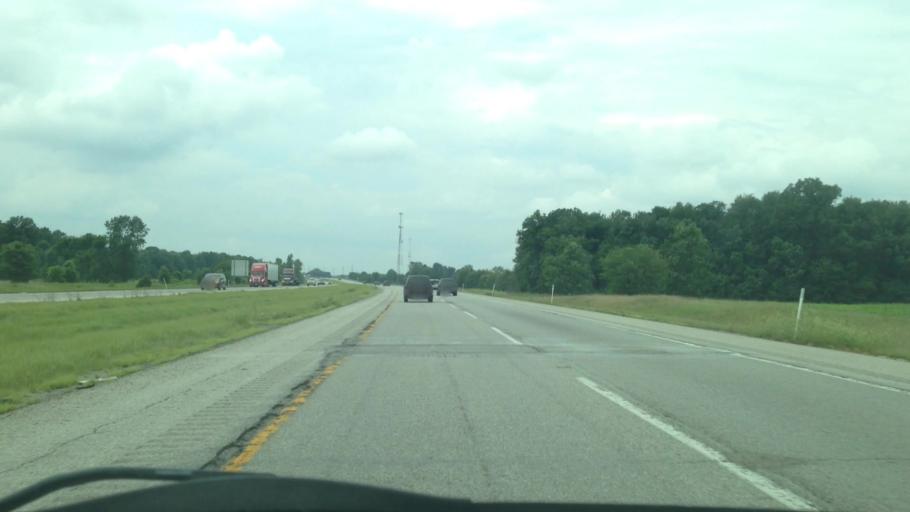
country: US
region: Indiana
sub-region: Elkhart County
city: Middlebury
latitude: 41.7457
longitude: -85.7152
